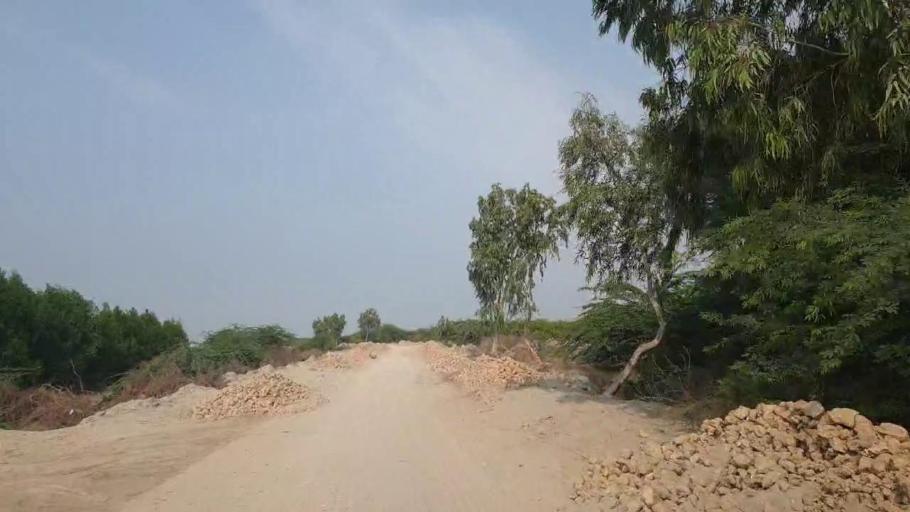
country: PK
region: Sindh
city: Badin
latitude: 24.6026
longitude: 68.7414
